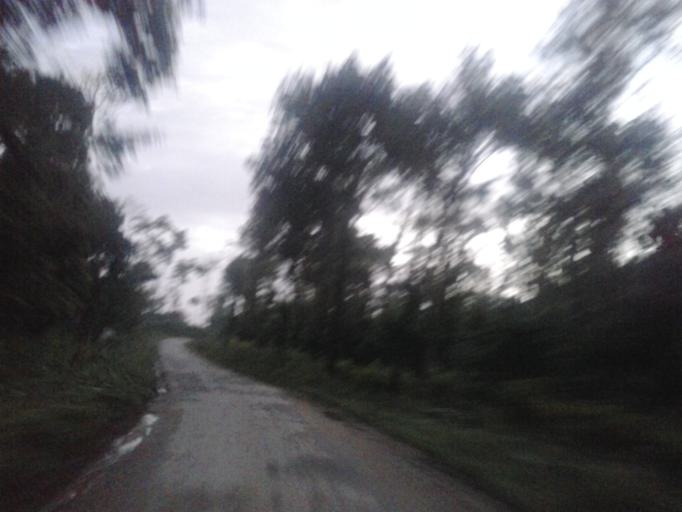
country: IN
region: Karnataka
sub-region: Hassan
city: Sakleshpur
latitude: 13.0029
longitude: 75.6883
